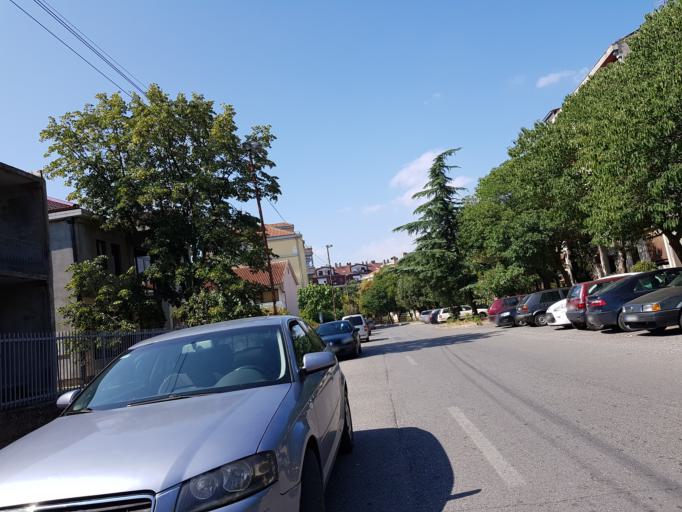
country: ME
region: Podgorica
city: Podgorica
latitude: 42.4325
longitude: 19.2772
